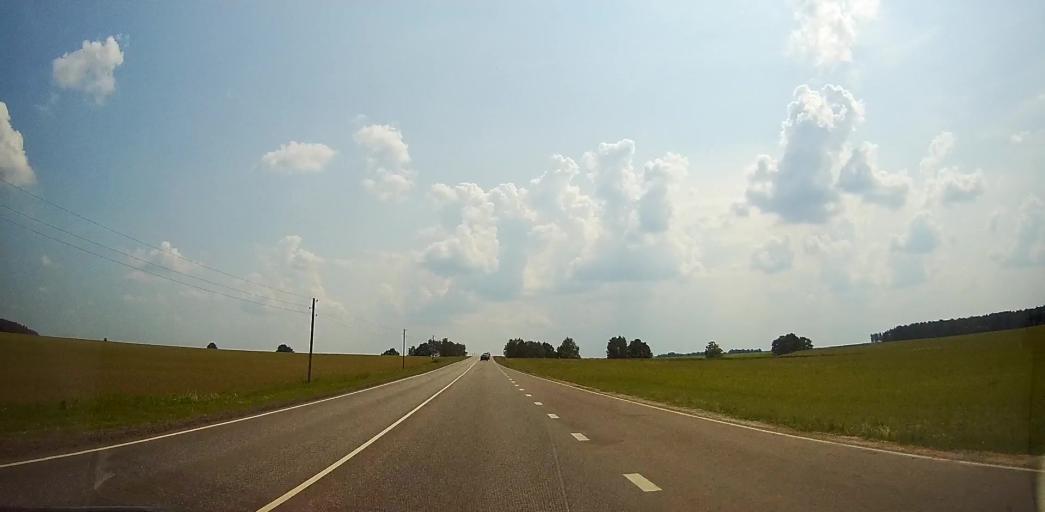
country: RU
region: Moskovskaya
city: Malino
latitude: 55.0458
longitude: 38.1492
